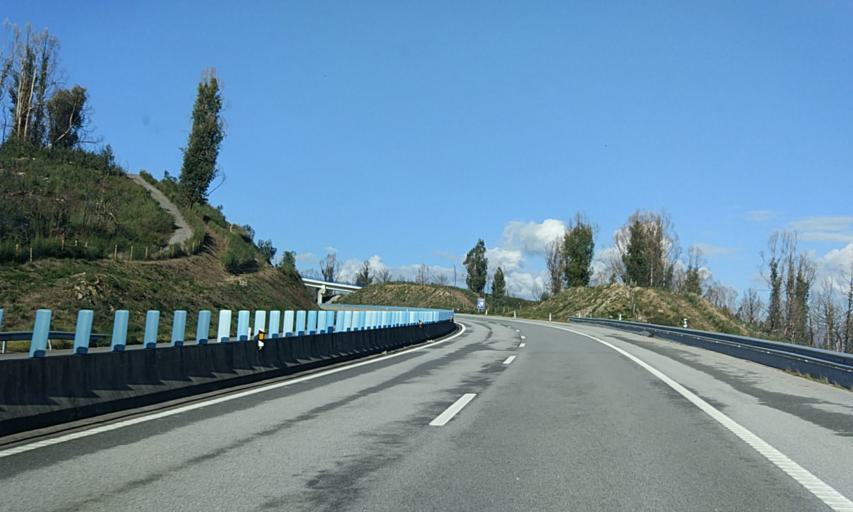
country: PT
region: Viseu
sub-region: Vouzela
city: Vouzela
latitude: 40.6994
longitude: -8.1018
